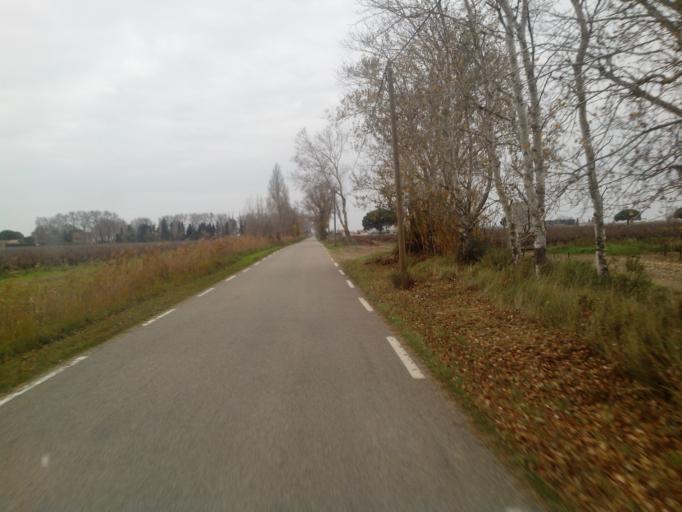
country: FR
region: Languedoc-Roussillon
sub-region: Departement du Gard
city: Vauvert
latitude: 43.5800
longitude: 4.3342
